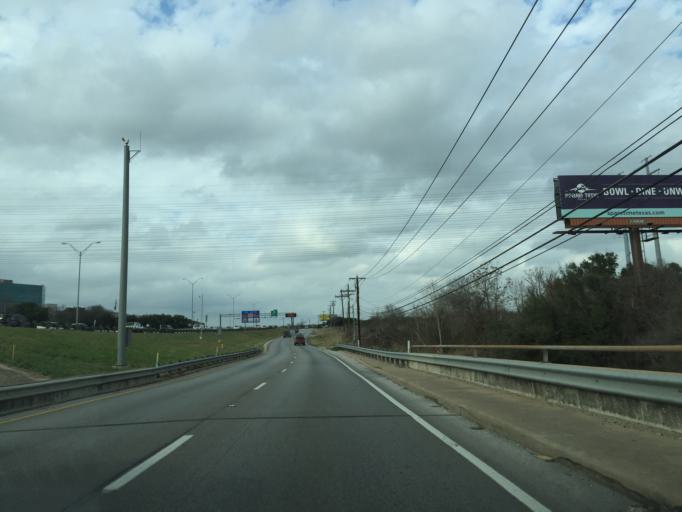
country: US
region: Texas
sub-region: Travis County
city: Wells Branch
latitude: 30.3884
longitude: -97.6720
